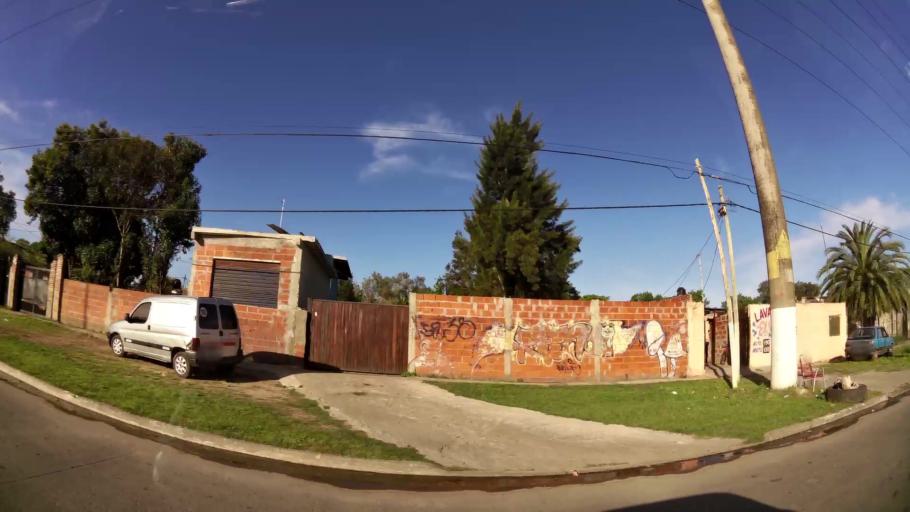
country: AR
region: Buenos Aires
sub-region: Partido de Quilmes
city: Quilmes
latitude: -34.8125
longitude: -58.2010
